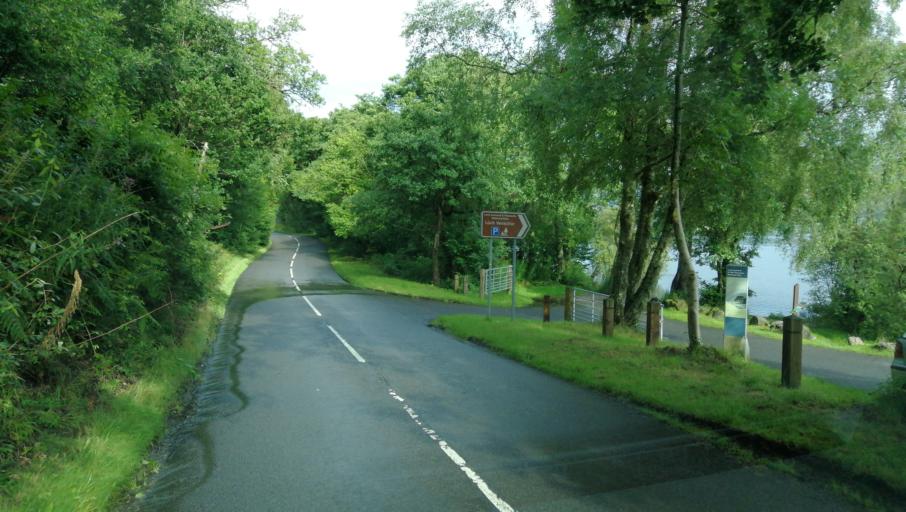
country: GB
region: Scotland
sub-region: Stirling
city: Callander
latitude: 56.2267
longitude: -4.3199
